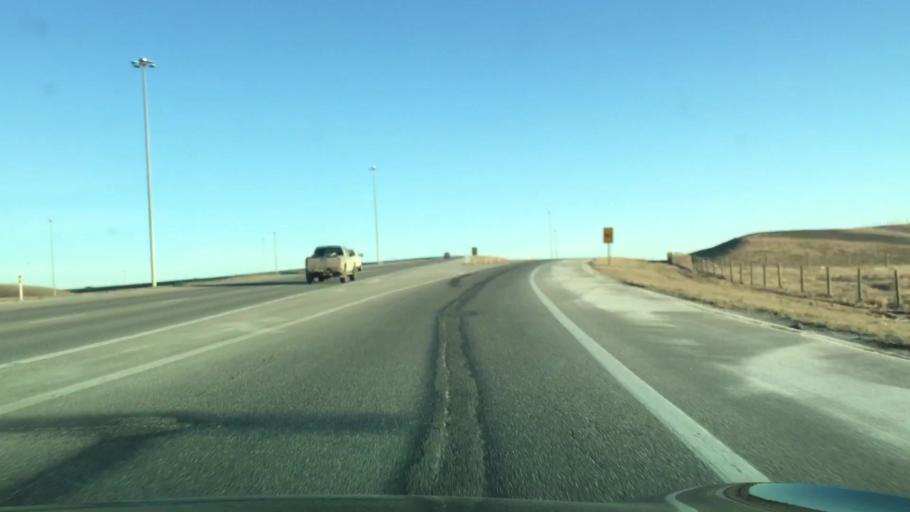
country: CA
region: Alberta
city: Airdrie
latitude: 51.1748
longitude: -114.0072
